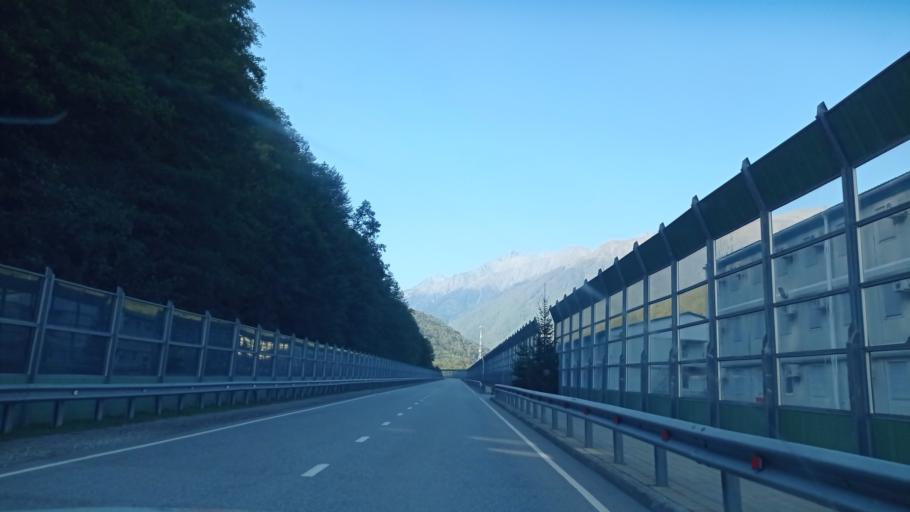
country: RU
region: Krasnodarskiy
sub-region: Sochi City
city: Krasnaya Polyana
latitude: 43.6865
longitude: 40.2759
